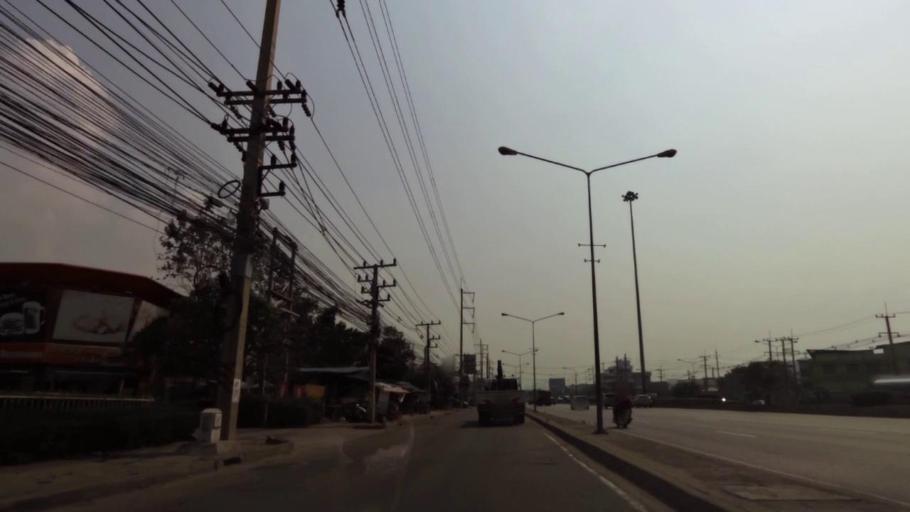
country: TH
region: Chon Buri
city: Chon Buri
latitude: 13.4119
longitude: 101.0000
